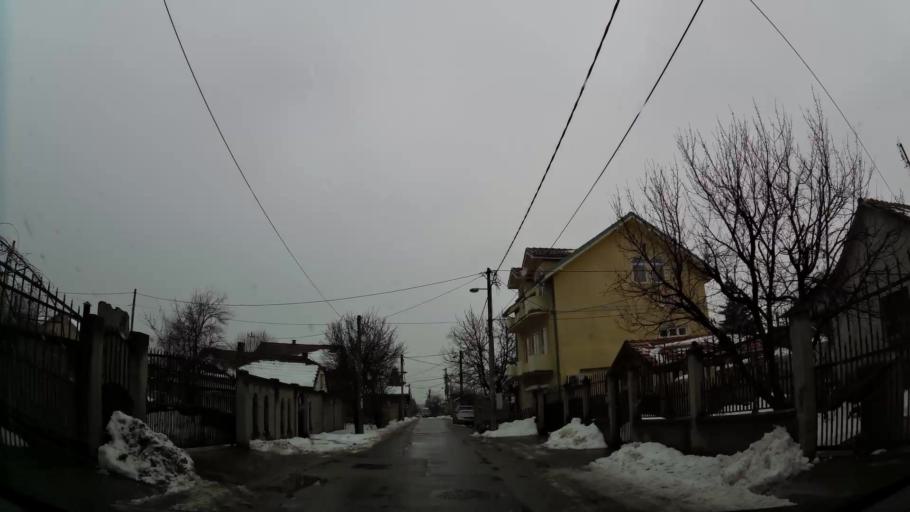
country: RS
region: Central Serbia
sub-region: Belgrade
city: Zemun
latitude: 44.8454
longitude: 20.3620
